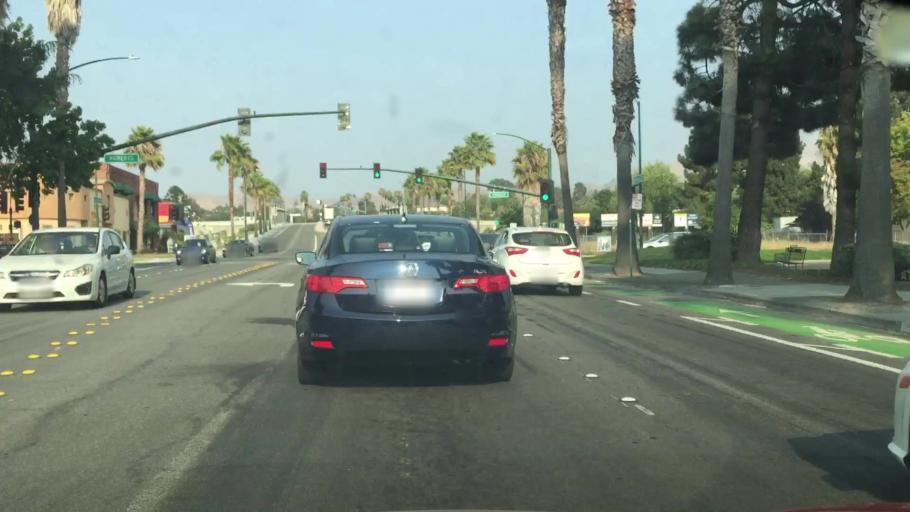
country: US
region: California
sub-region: Alameda County
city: Fremont
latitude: 37.5328
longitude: -121.9571
